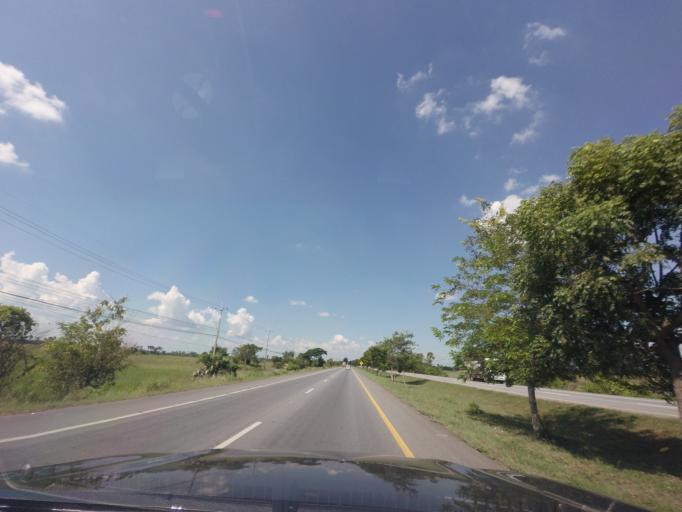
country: TH
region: Nakhon Ratchasima
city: Non Sung
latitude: 15.1330
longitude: 102.3086
